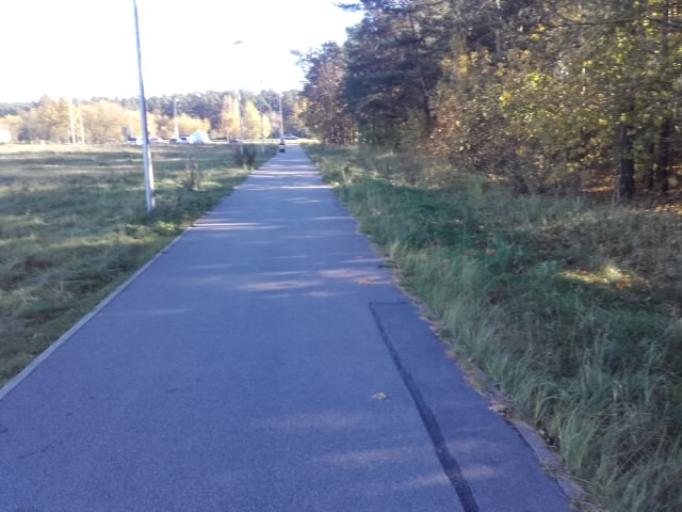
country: LV
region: Stopini
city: Ulbroka
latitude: 56.9367
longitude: 24.2198
